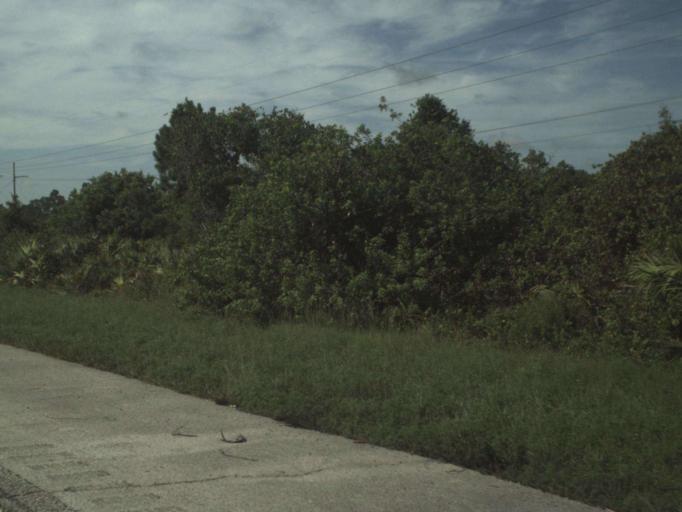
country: US
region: Florida
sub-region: Indian River County
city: West Vero Corridor
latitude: 27.6704
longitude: -80.5308
